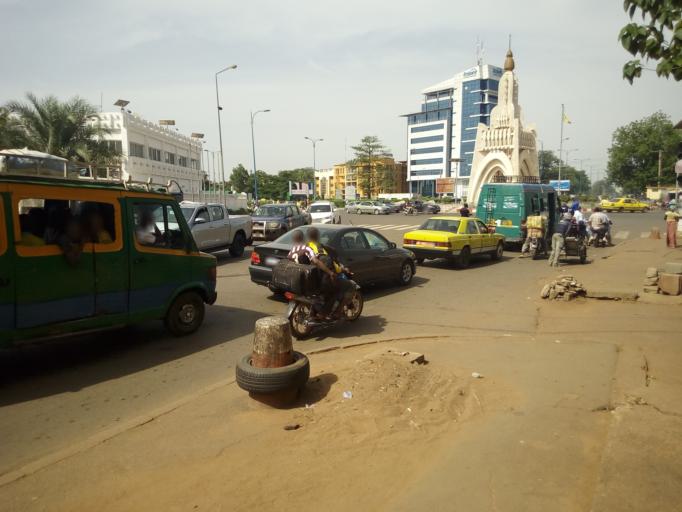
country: ML
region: Bamako
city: Bamako
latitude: 12.6377
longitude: -8.0042
